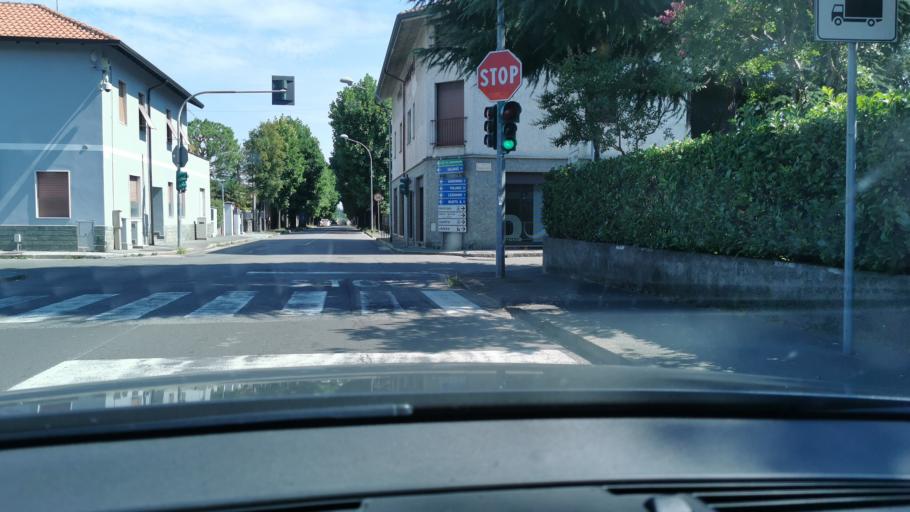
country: IT
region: Lombardy
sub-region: Citta metropolitana di Milano
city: Rescaldina
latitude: 45.6191
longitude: 8.9549
